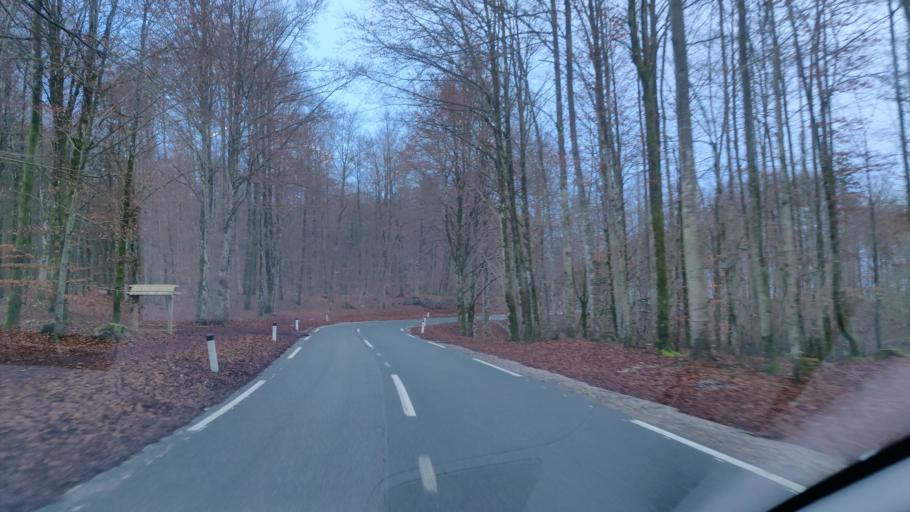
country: SI
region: Bohinj
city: Bohinjska Bistrica
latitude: 46.2815
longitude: 13.8502
